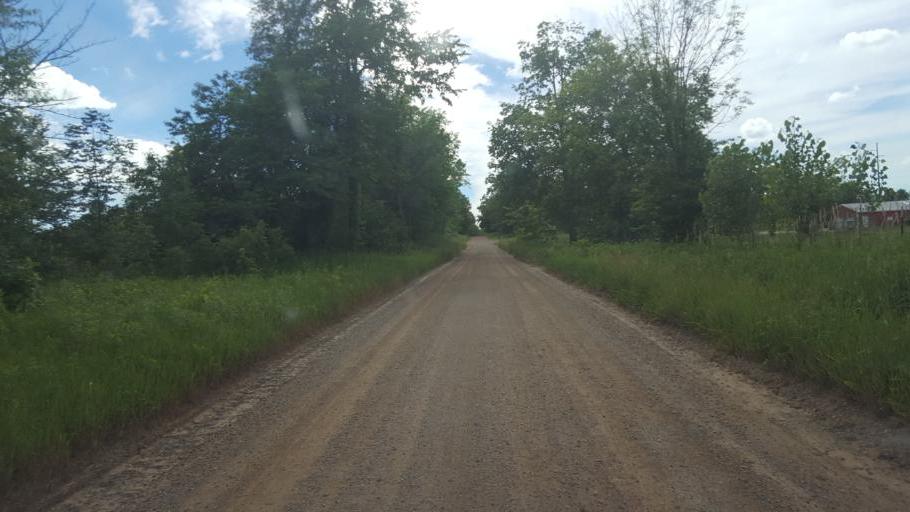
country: US
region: Michigan
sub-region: Barry County
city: Nashville
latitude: 42.5971
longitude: -84.9734
